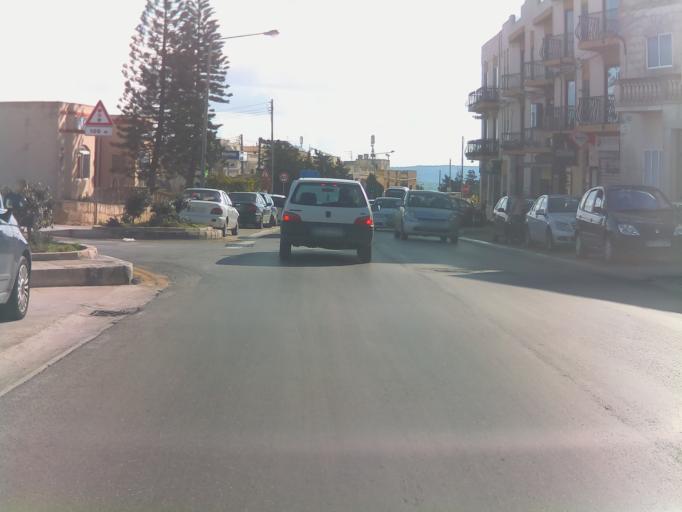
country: MT
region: Il-Mellieha
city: Mellieha
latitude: 35.9555
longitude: 14.3699
